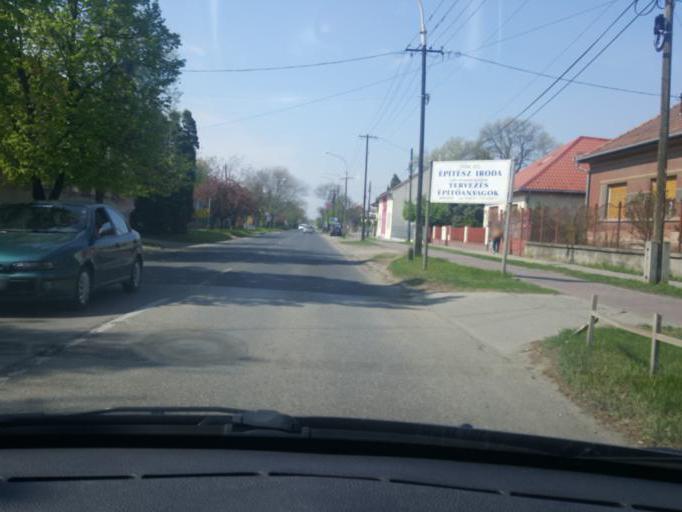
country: HU
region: Pest
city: Monor
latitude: 47.3514
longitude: 19.4430
